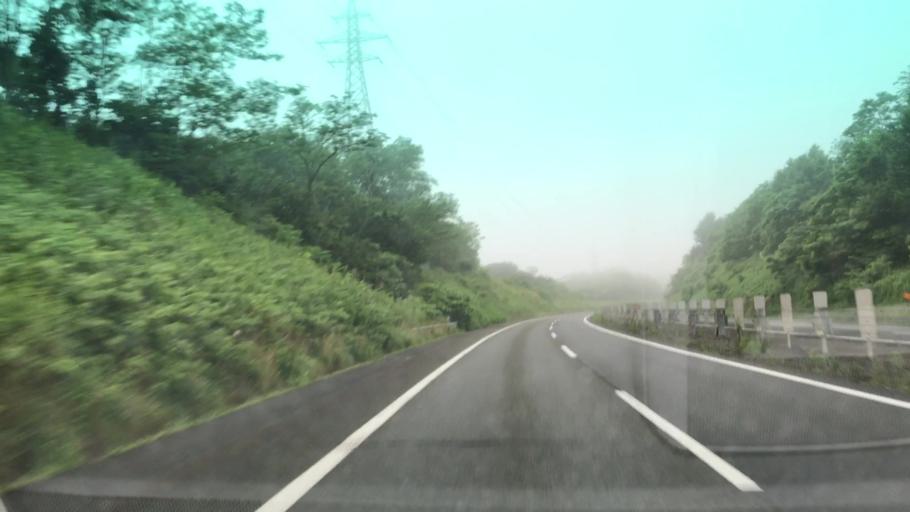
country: JP
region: Hokkaido
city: Tomakomai
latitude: 42.6655
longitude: 141.6102
